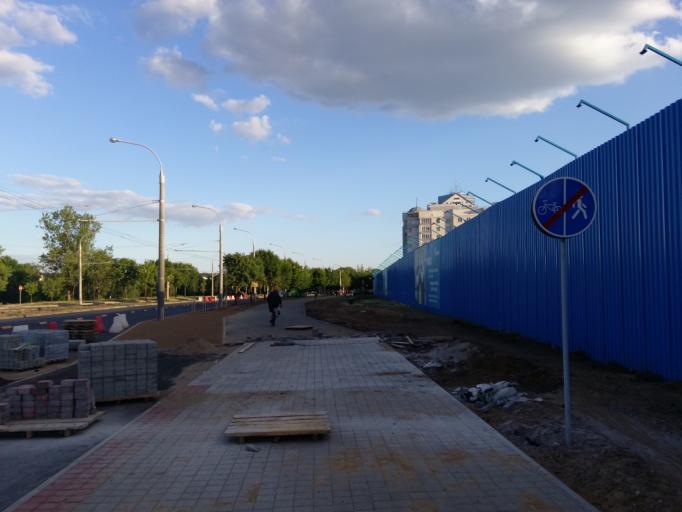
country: BY
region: Minsk
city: Minsk
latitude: 53.9281
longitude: 27.6392
